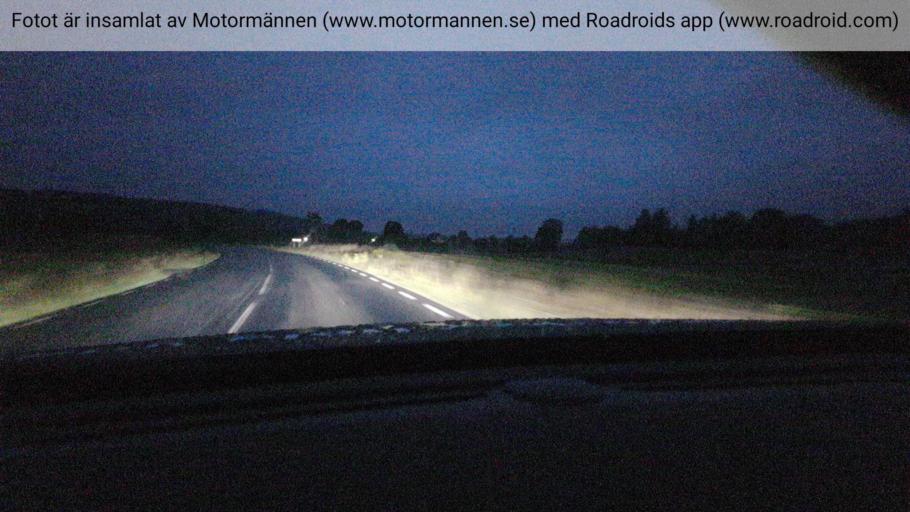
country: SE
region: Vaestra Goetaland
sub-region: Falkopings Kommun
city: Akarp
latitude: 58.2830
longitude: 13.7106
